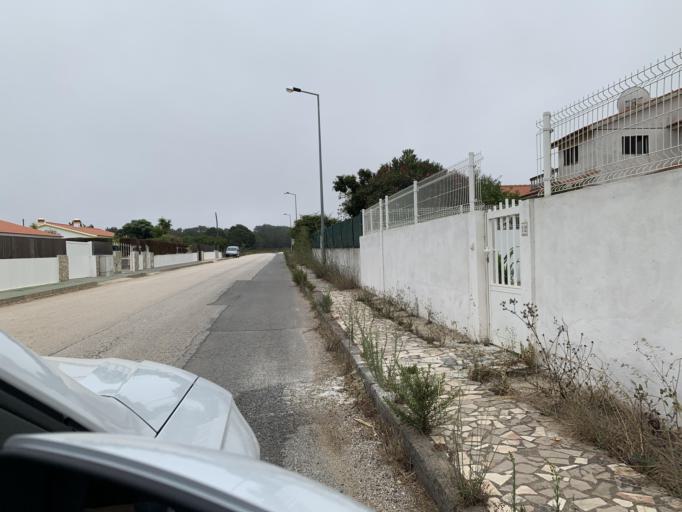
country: PT
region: Faro
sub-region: Aljezur
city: Aljezur
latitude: 37.3021
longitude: -8.8480
